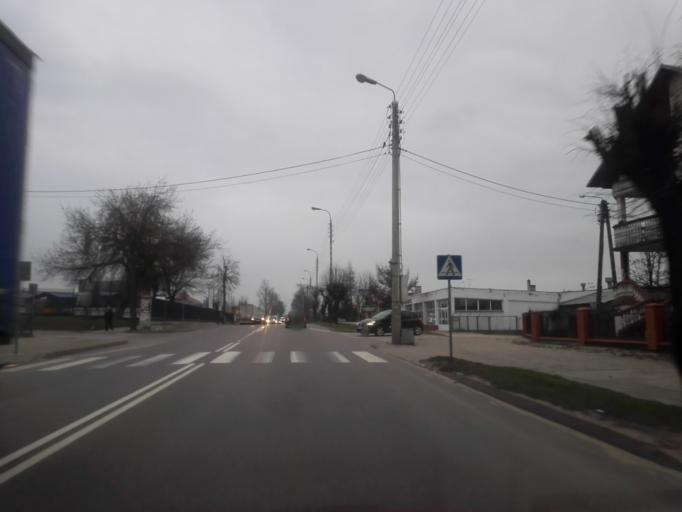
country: PL
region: Podlasie
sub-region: Powiat grajewski
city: Grajewo
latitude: 53.6441
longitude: 22.4482
